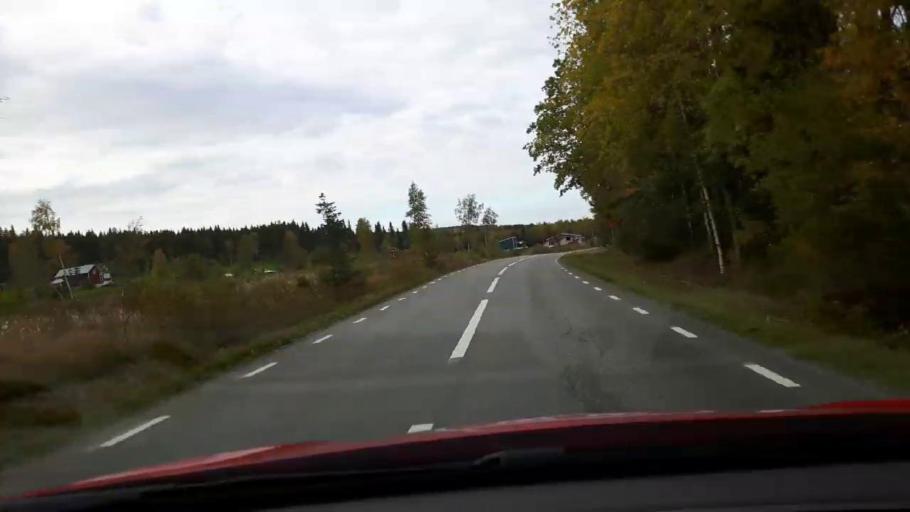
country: SE
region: Jaemtland
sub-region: Krokoms Kommun
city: Krokom
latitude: 63.1675
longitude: 14.1112
